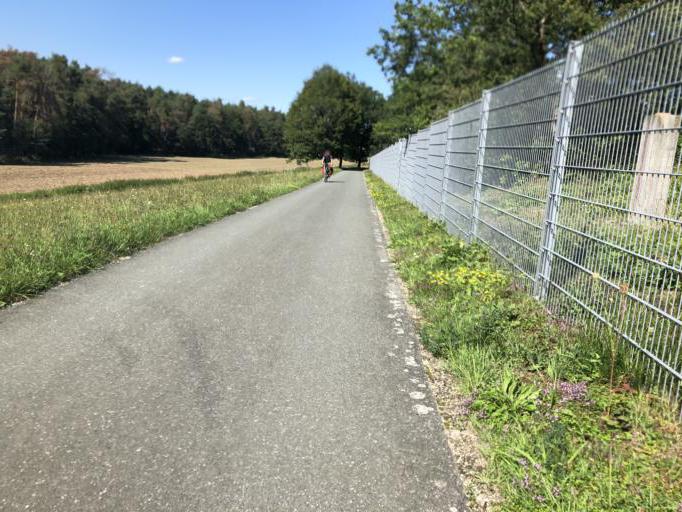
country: DE
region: Bavaria
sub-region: Regierungsbezirk Mittelfranken
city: Mohrendorf
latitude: 49.6231
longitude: 10.9786
